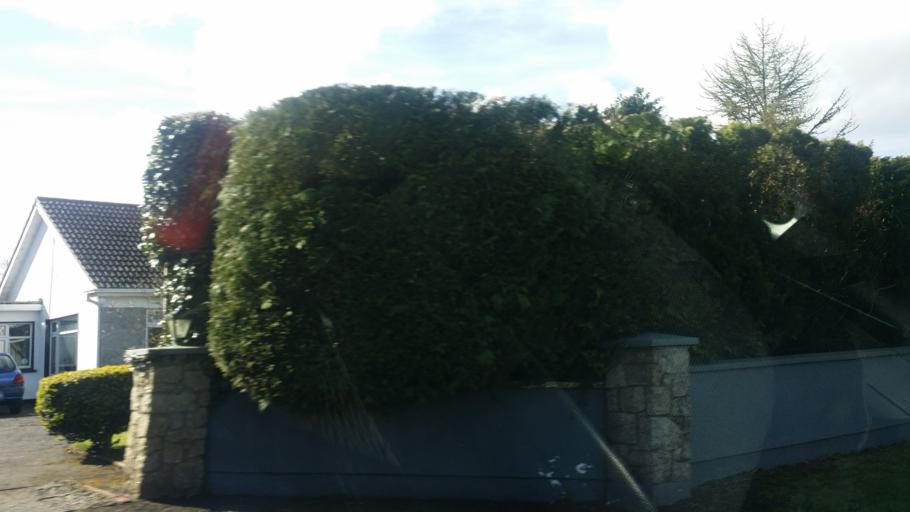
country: IE
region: Leinster
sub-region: An Mhi
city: Kells
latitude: 53.7192
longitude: -6.8888
